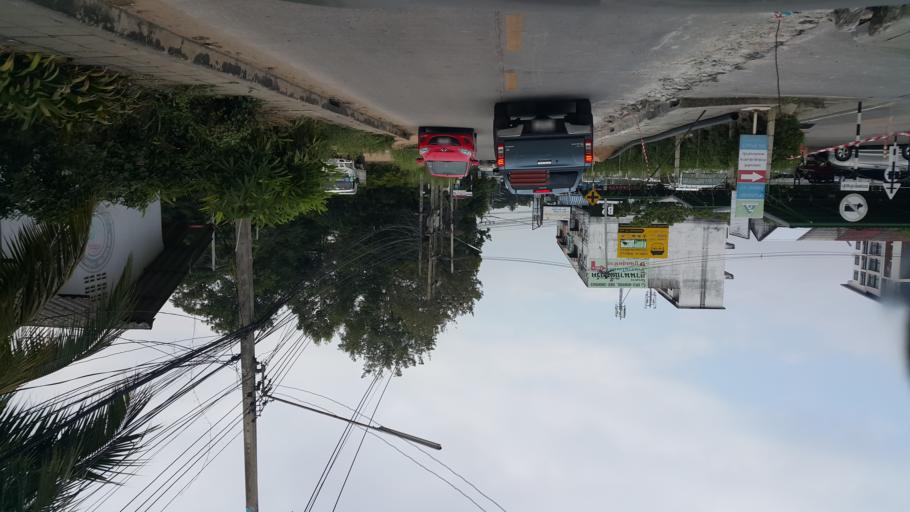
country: TH
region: Chiang Mai
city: Chiang Mai
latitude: 18.8157
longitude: 98.9920
